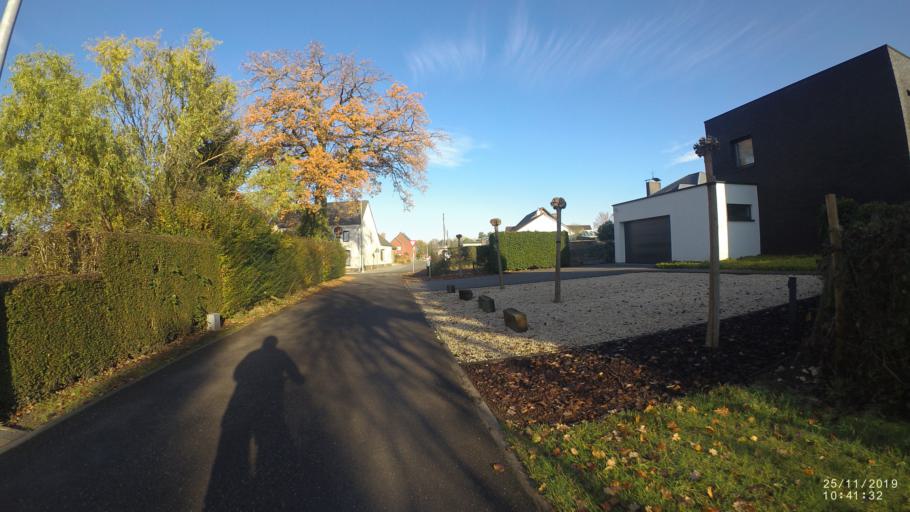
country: BE
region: Flanders
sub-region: Provincie Vlaams-Brabant
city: Scherpenheuvel-Zichem
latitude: 51.0108
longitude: 4.9514
